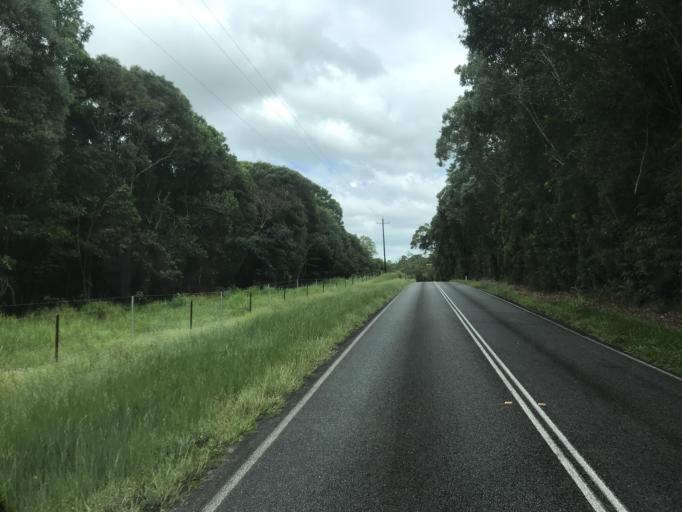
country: AU
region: Queensland
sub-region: Cassowary Coast
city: Innisfail
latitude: -17.8474
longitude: 146.0579
